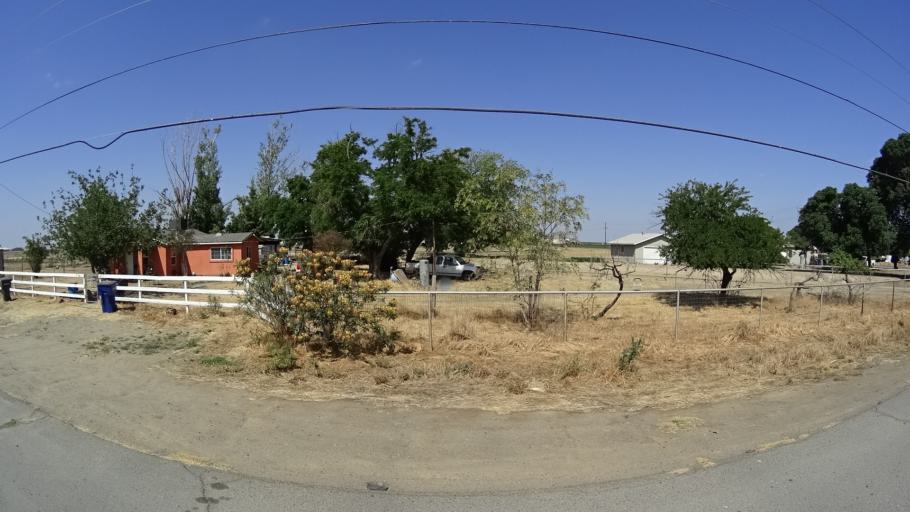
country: US
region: California
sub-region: Kings County
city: Home Garden
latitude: 36.2835
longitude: -119.6370
